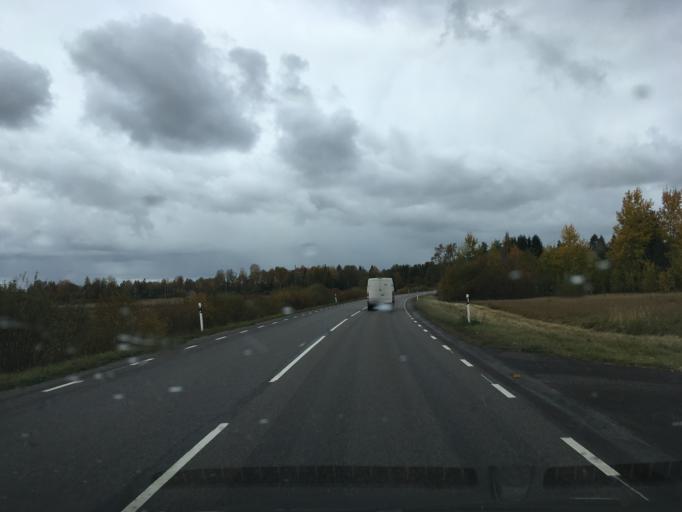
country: EE
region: Harju
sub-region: Anija vald
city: Kehra
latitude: 59.3308
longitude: 25.3167
